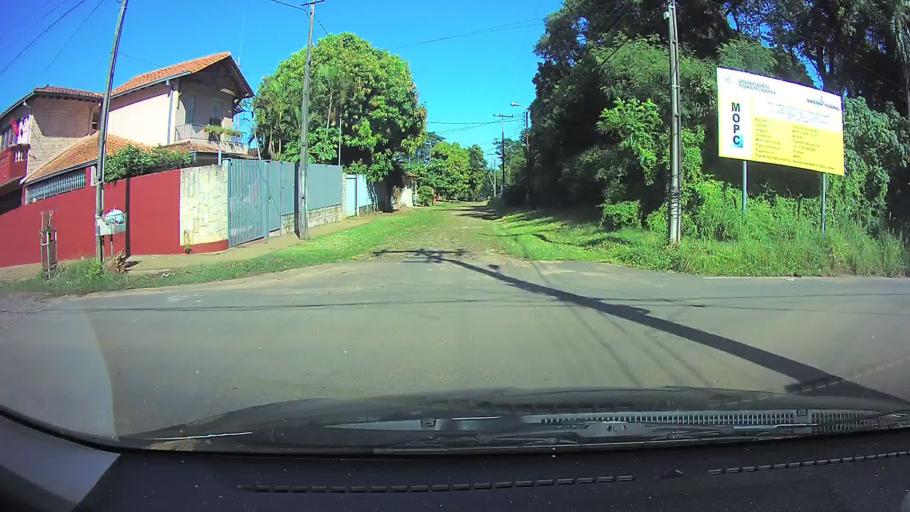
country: PY
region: Central
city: Fernando de la Mora
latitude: -25.2764
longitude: -57.5148
